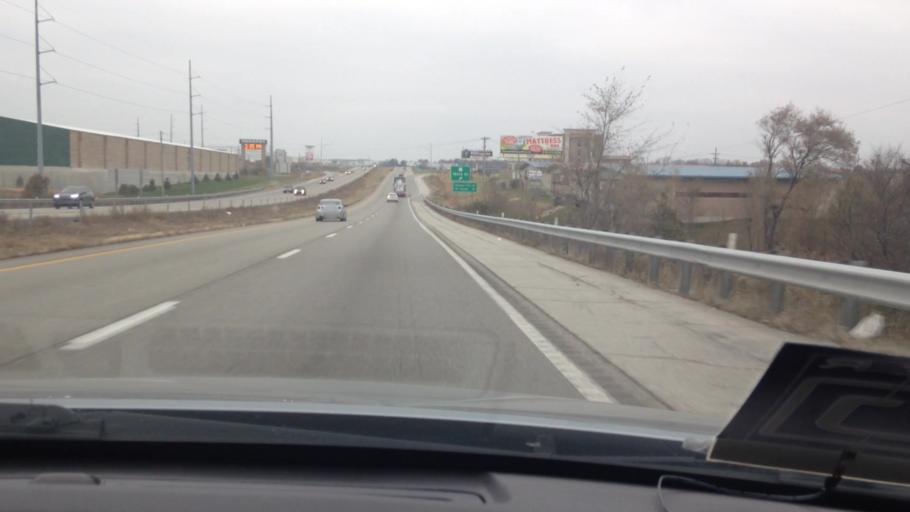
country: US
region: Missouri
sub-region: Cass County
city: Belton
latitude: 38.8211
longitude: -94.5144
